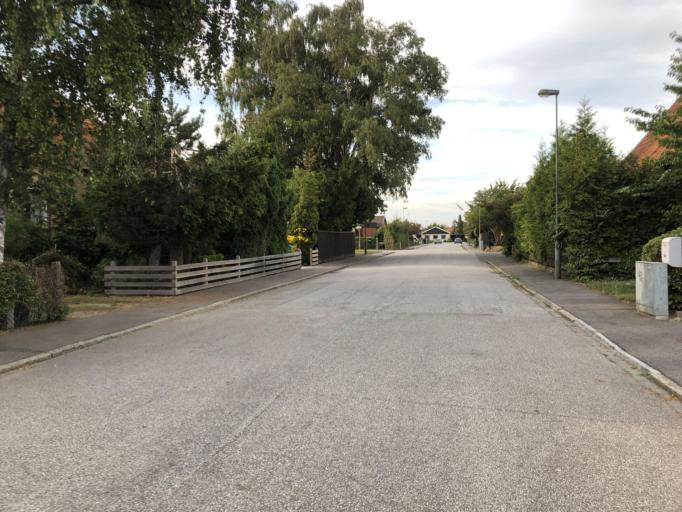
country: SE
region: Skane
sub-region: Burlovs Kommun
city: Arloev
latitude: 55.5922
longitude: 13.0795
